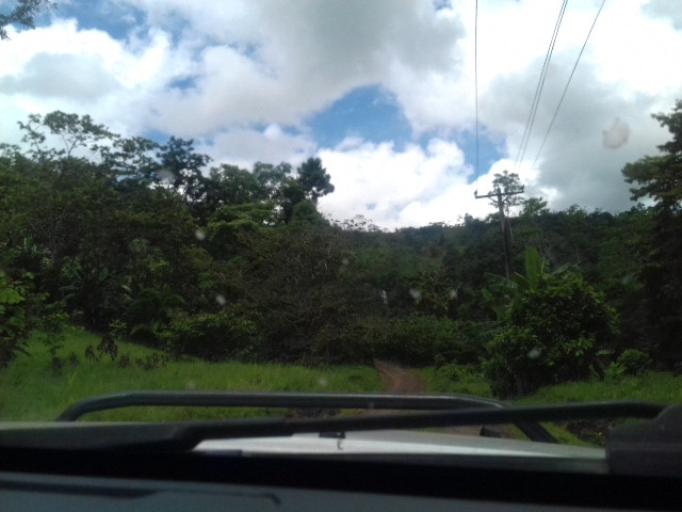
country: NI
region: Matagalpa
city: Rio Blanco
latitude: 13.0325
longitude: -85.2315
